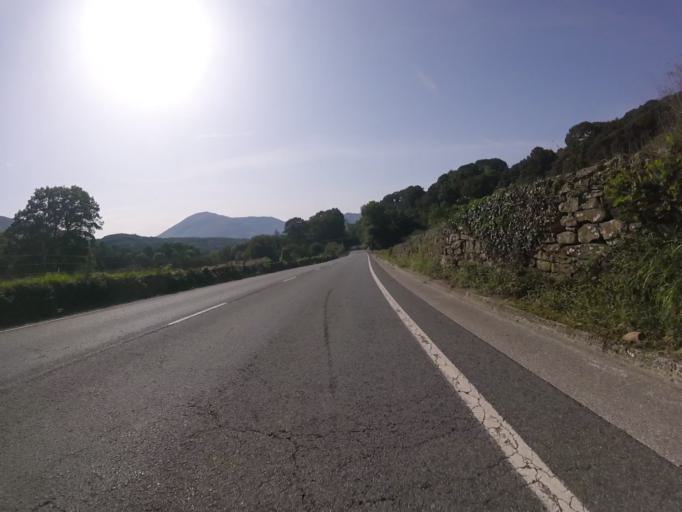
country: ES
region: Navarre
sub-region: Provincia de Navarra
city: Zugarramurdi
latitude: 43.2043
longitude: -1.4859
